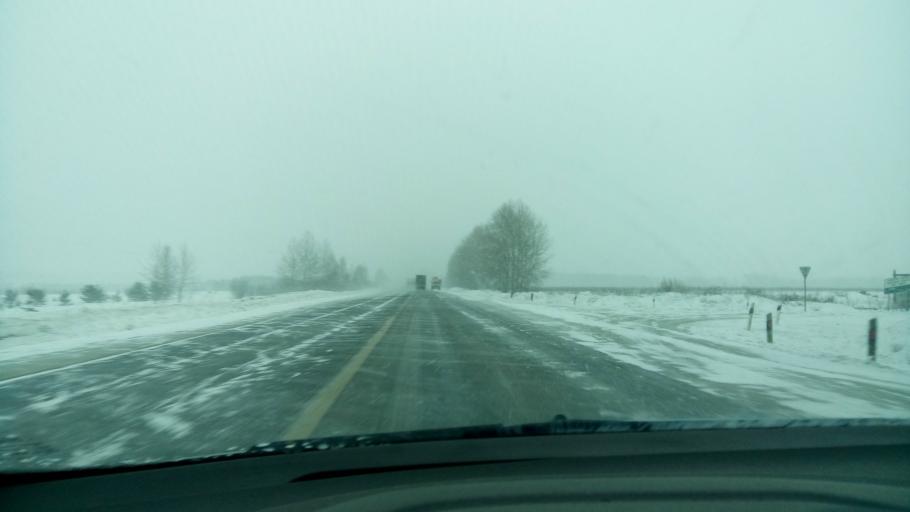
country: RU
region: Sverdlovsk
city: Beloyarskiy
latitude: 56.7745
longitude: 61.5213
